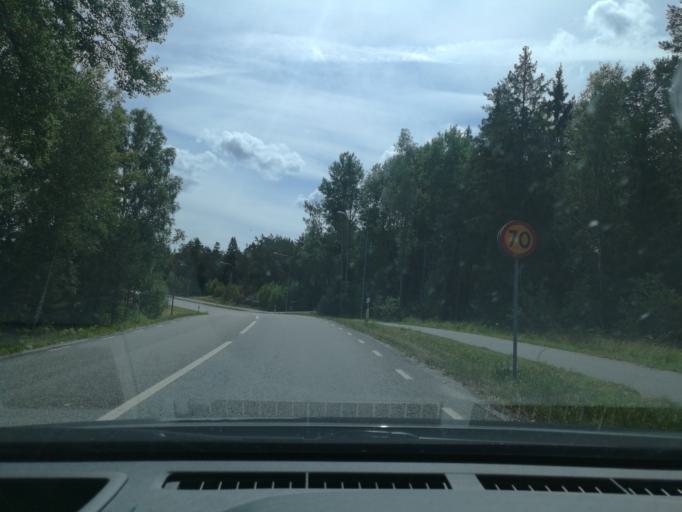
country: SE
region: Stockholm
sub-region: Sigtuna Kommun
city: Rosersberg
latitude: 59.6003
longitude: 17.8819
